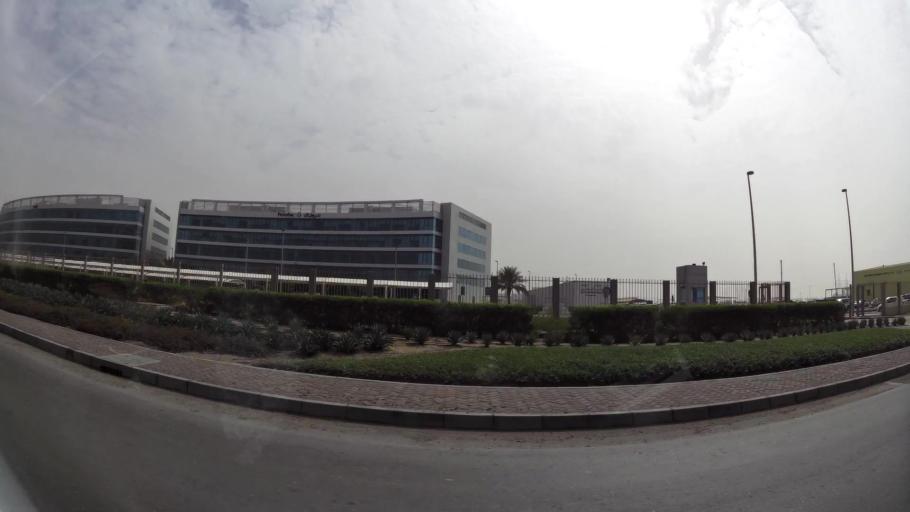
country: AE
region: Abu Dhabi
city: Abu Dhabi
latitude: 24.3239
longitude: 54.5196
